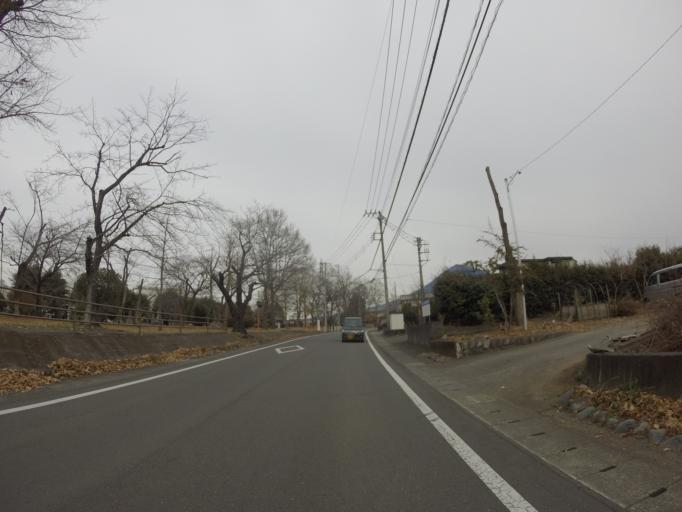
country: JP
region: Shizuoka
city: Fujinomiya
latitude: 35.2379
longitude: 138.6235
